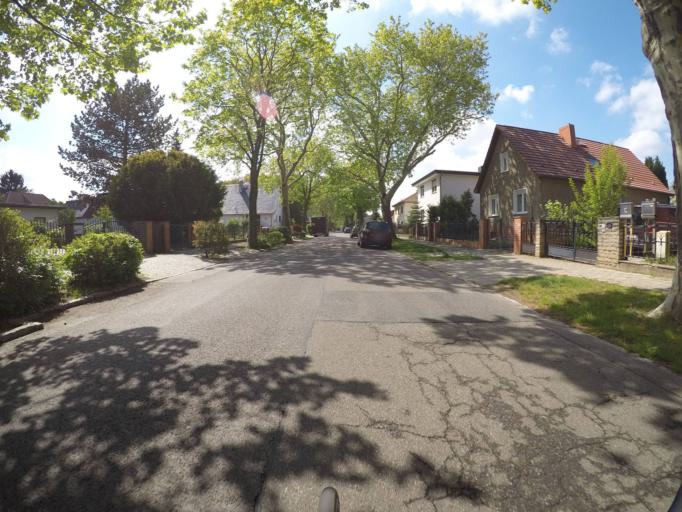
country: DE
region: Berlin
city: Biesdorf
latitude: 52.5262
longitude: 13.5552
